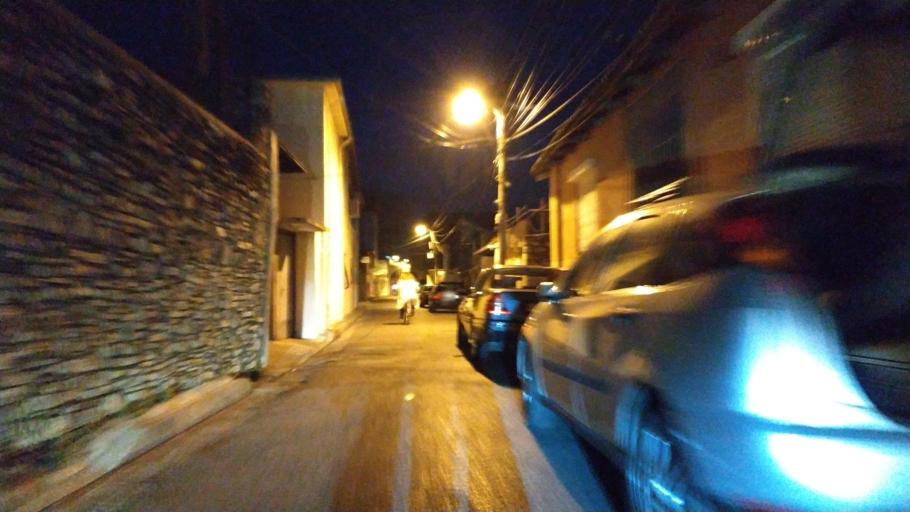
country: AL
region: Shkoder
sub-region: Rrethi i Shkodres
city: Shkoder
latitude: 42.0675
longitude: 19.5085
